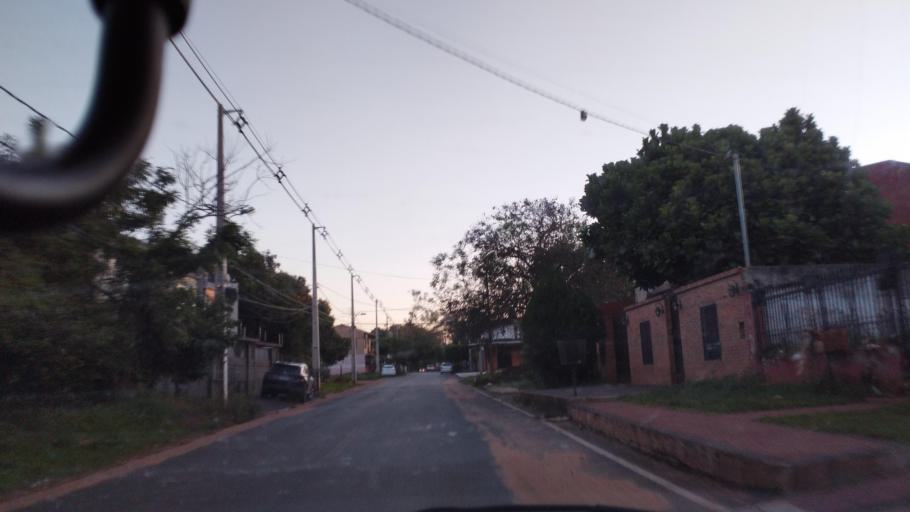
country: PY
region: Central
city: Fernando de la Mora
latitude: -25.2991
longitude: -57.5149
